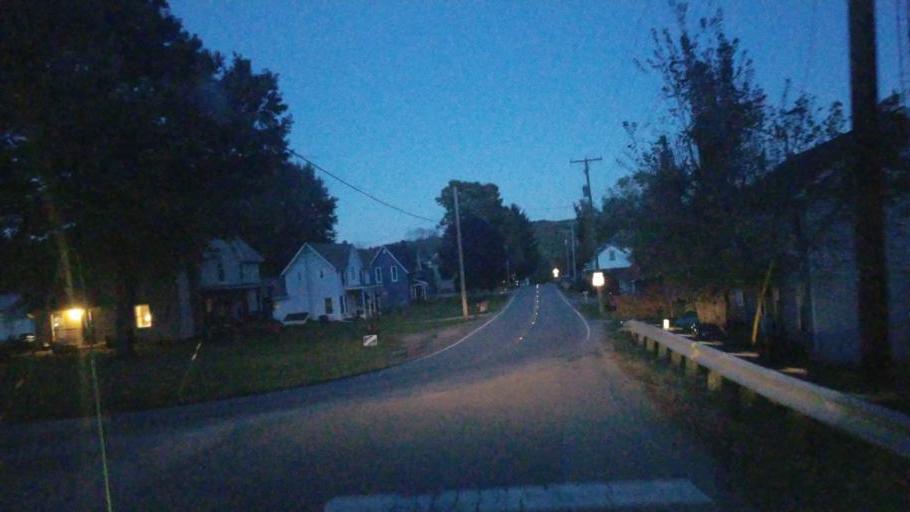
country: US
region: Ohio
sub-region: Perry County
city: Somerset
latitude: 39.8780
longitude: -82.2202
